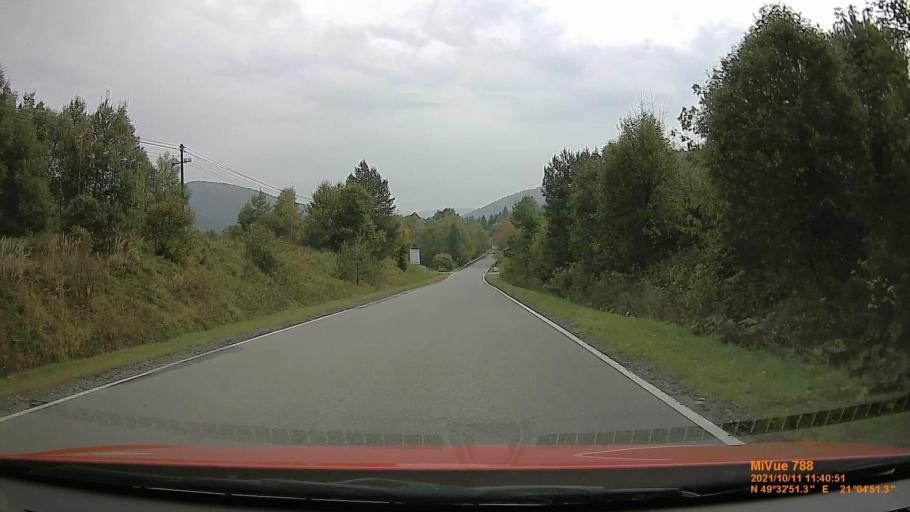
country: PL
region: Lesser Poland Voivodeship
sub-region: Powiat gorlicki
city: Ropa
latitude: 49.5476
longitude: 21.0811
